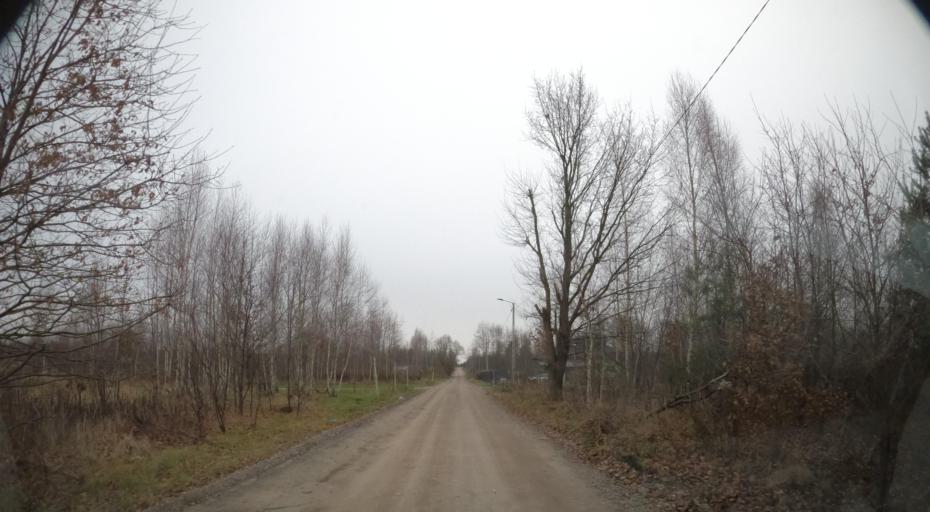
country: PL
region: Masovian Voivodeship
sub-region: Powiat radomski
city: Jastrzebia
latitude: 51.4853
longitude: 21.1899
